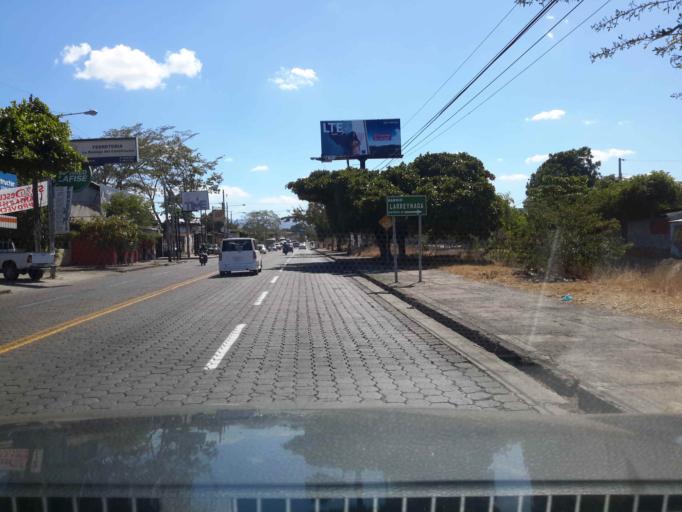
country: NI
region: Managua
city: Managua
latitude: 12.1439
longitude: -86.2417
